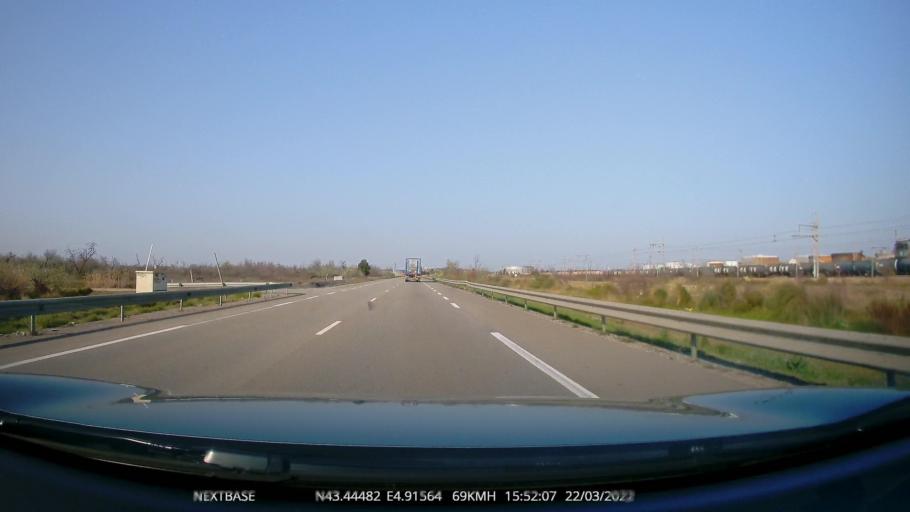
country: FR
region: Provence-Alpes-Cote d'Azur
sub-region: Departement des Bouches-du-Rhone
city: Fos-sur-Mer
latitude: 43.4450
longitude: 4.9157
